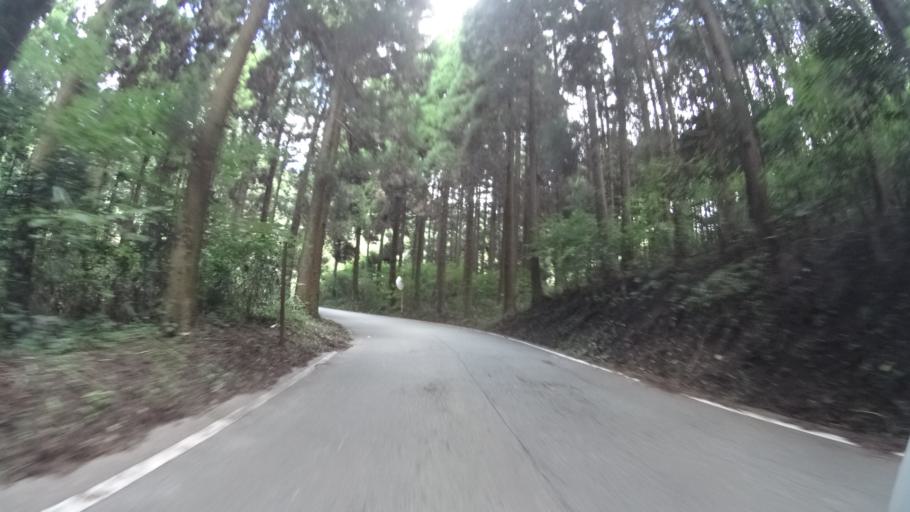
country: JP
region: Kumamoto
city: Aso
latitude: 32.8097
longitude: 131.1332
